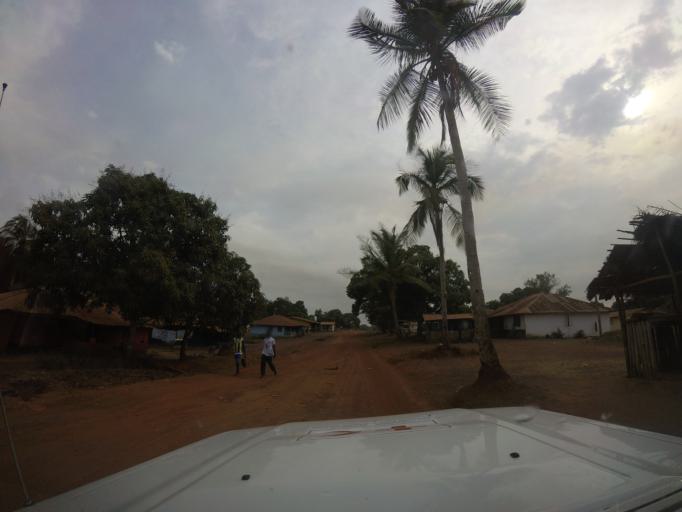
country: LR
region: Grand Cape Mount
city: Robertsport
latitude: 6.9732
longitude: -11.3093
